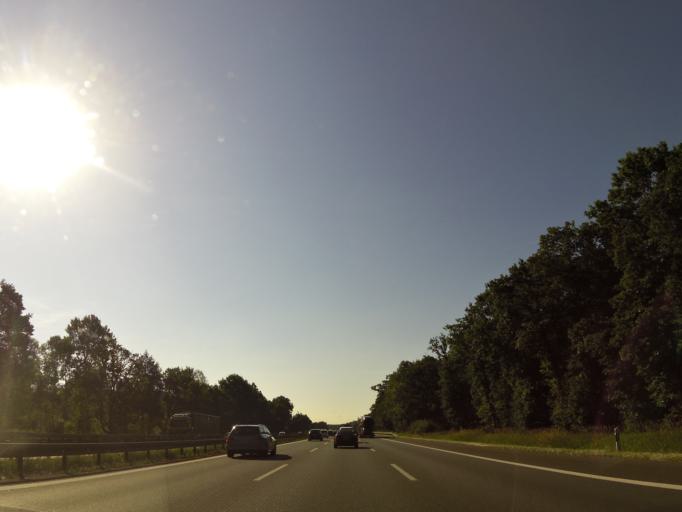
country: DE
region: Bavaria
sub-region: Regierungsbezirk Mittelfranken
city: Wetzendorf
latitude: 49.5209
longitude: 11.0767
